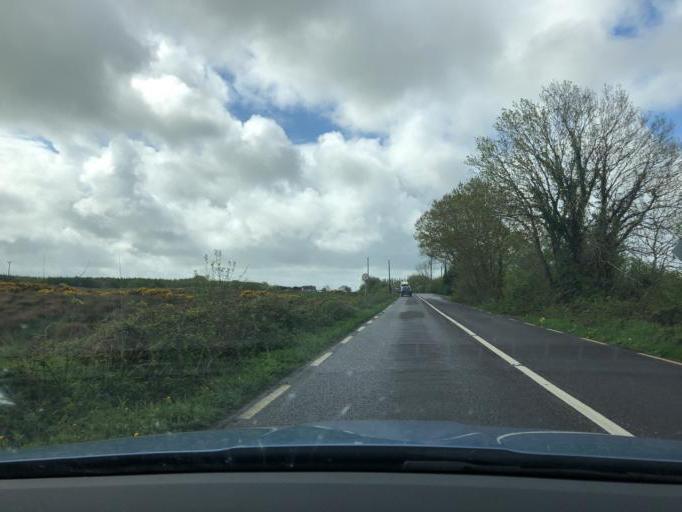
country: IE
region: Munster
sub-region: An Clar
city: Kilrush
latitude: 52.5504
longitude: -9.3813
